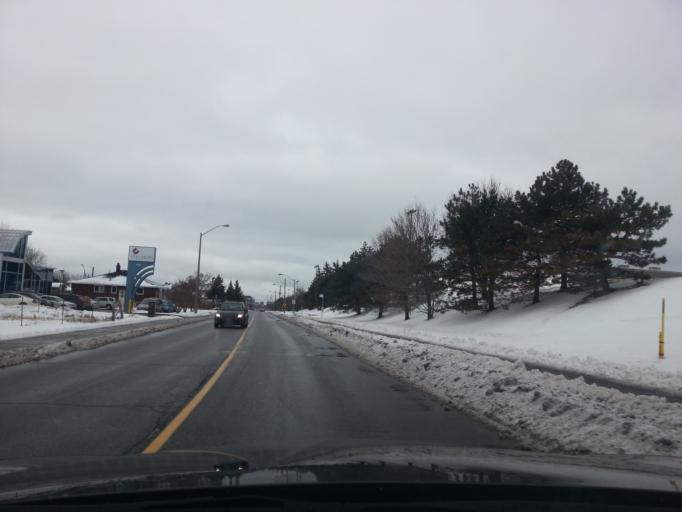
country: CA
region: Ontario
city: Ottawa
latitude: 45.4192
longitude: -75.6381
